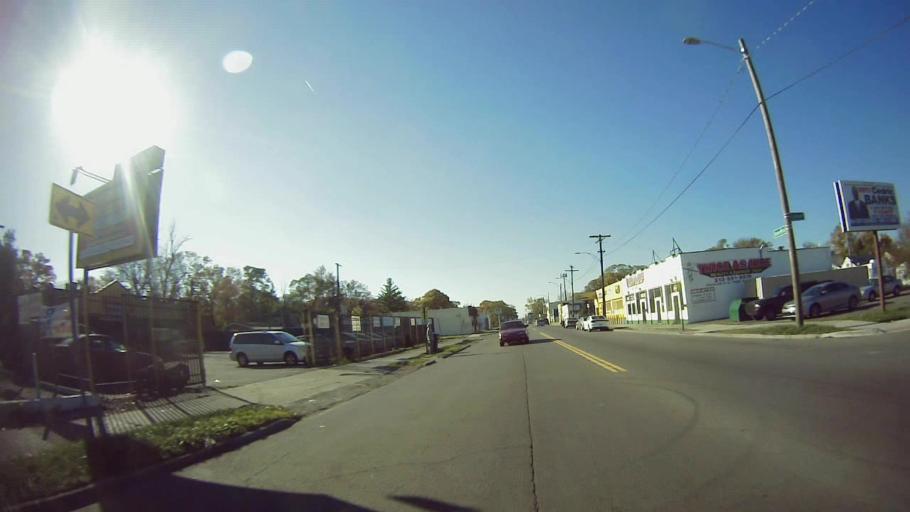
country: US
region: Michigan
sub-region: Wayne County
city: Hamtramck
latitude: 42.4333
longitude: -83.0539
